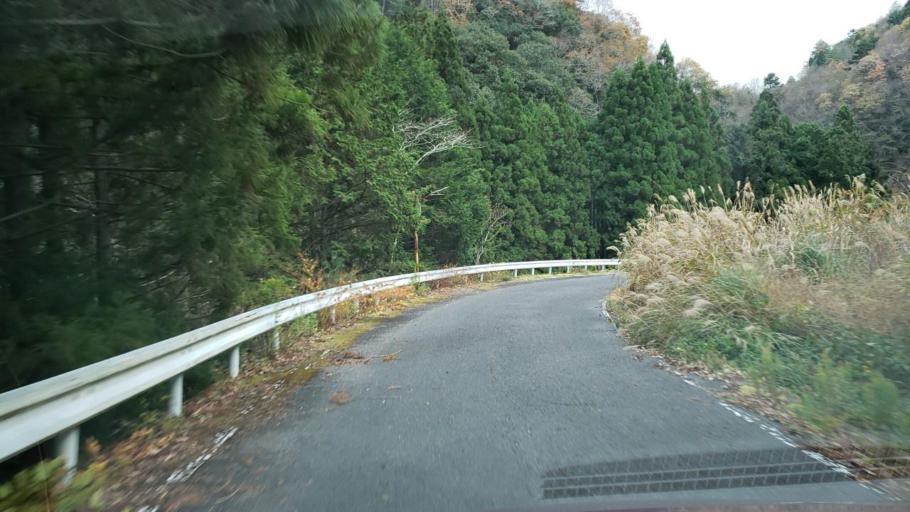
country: JP
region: Tokushima
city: Wakimachi
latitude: 34.1450
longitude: 134.2290
